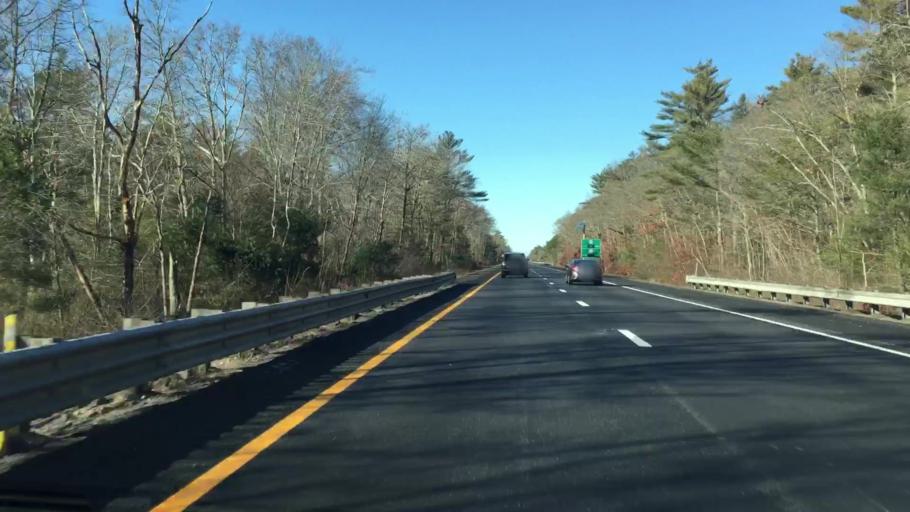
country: US
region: Massachusetts
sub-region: Plymouth County
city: West Wareham
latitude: 41.8184
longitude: -70.8004
